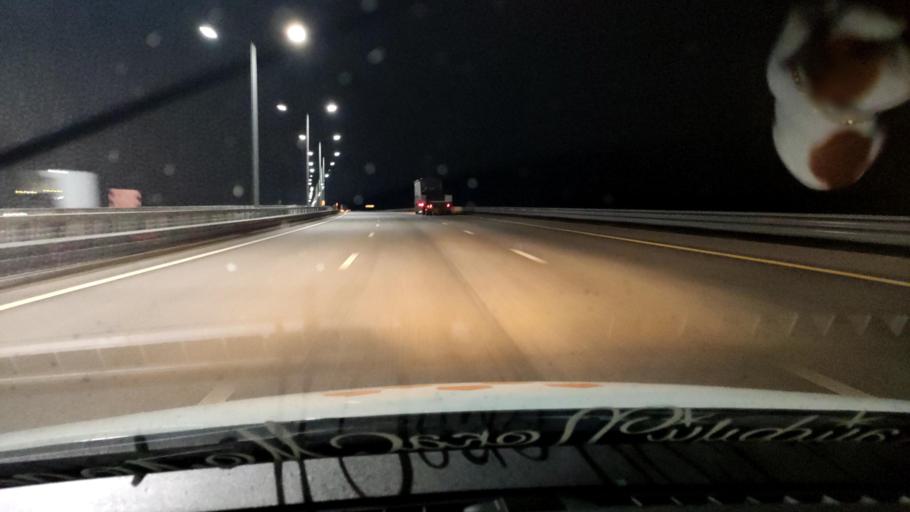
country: RU
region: Voronezj
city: Somovo
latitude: 51.7953
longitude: 39.2607
